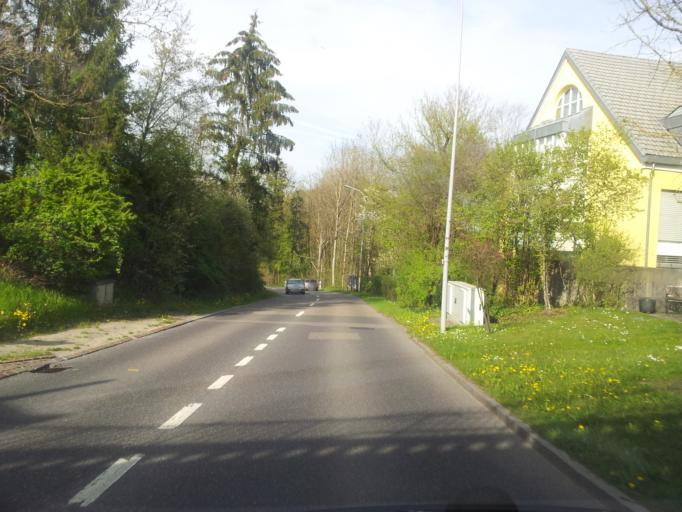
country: CH
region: Zurich
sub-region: Bezirk Uster
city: Gockhausen
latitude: 47.3821
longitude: 8.5991
